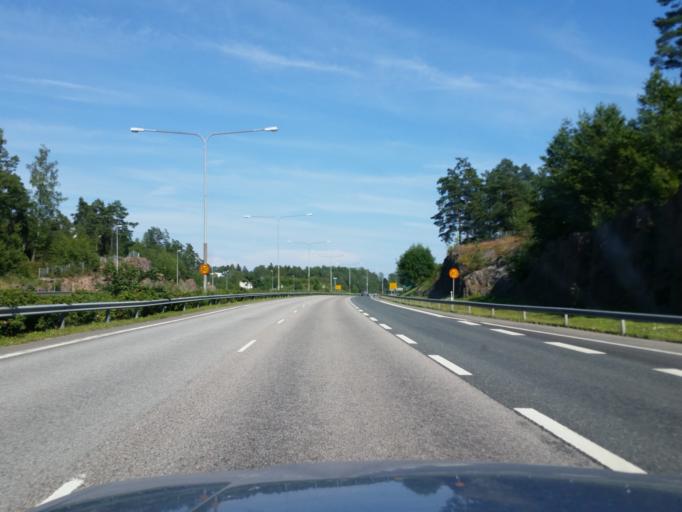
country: FI
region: Uusimaa
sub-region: Helsinki
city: Koukkuniemi
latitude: 60.1650
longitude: 24.7444
